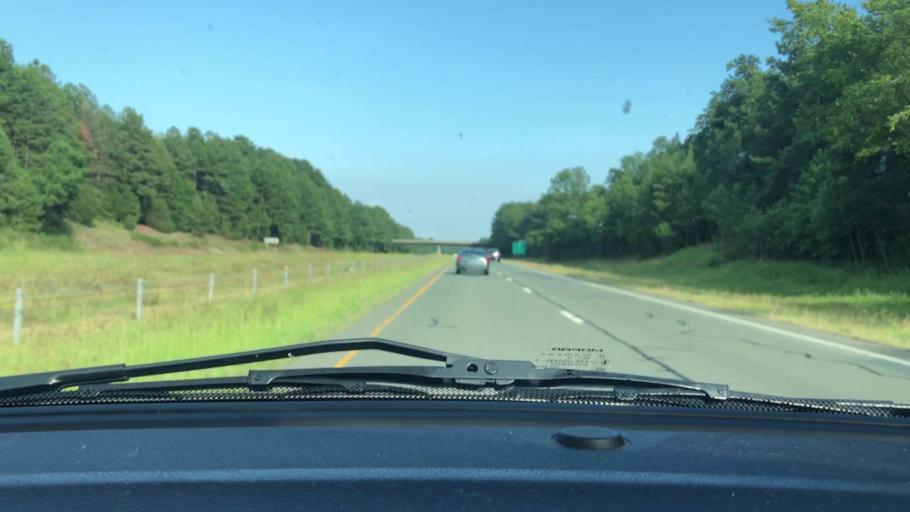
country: US
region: North Carolina
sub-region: Chatham County
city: Siler City
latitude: 35.7503
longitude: -79.4500
